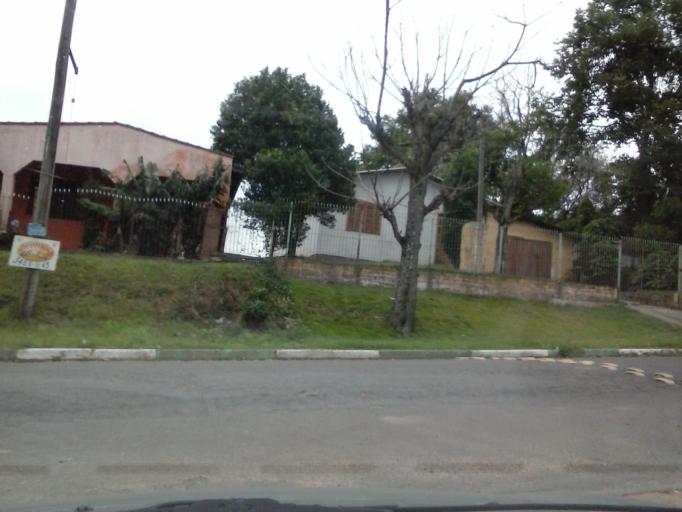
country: BR
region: Rio Grande do Sul
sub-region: Sapucaia Do Sul
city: Sapucaia
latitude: -29.8415
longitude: -51.1178
